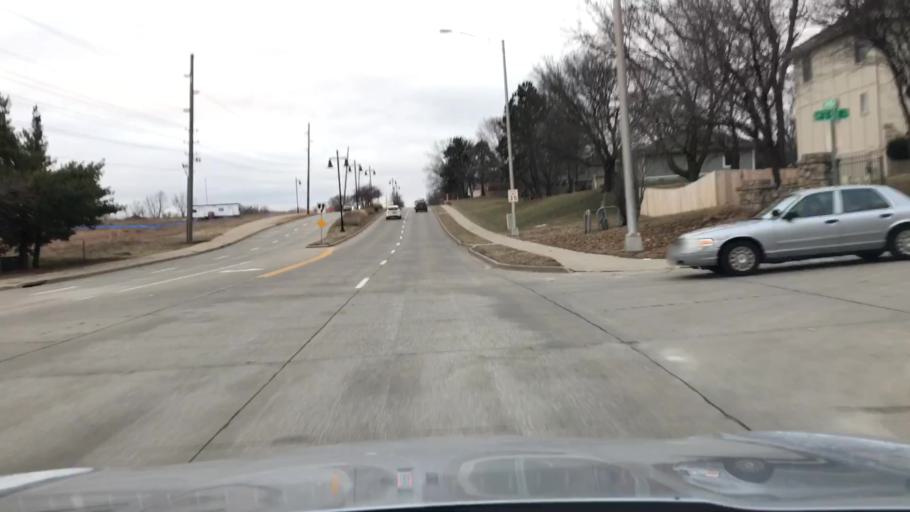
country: US
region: Missouri
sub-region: Jackson County
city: Lees Summit
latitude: 38.9151
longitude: -94.4133
